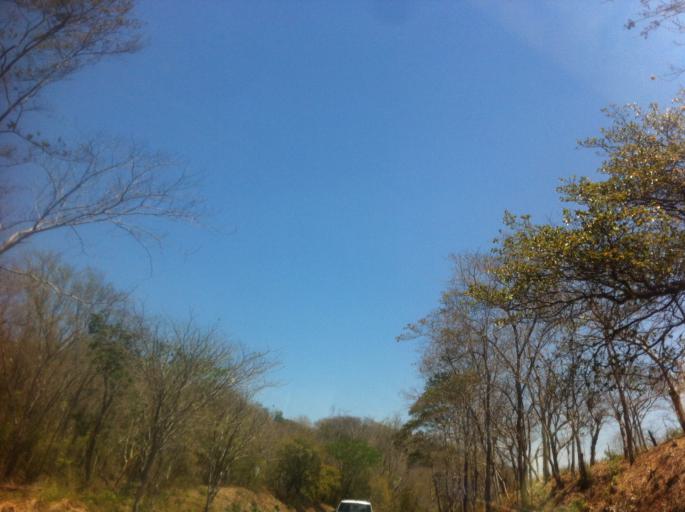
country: CR
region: Guanacaste
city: Belen
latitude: 10.3692
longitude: -85.5774
